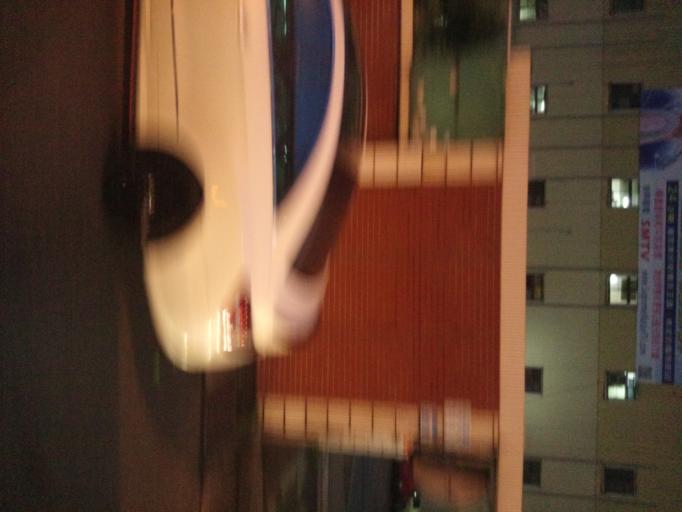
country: TW
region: Taiwan
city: Daxi
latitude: 24.9265
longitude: 121.2125
